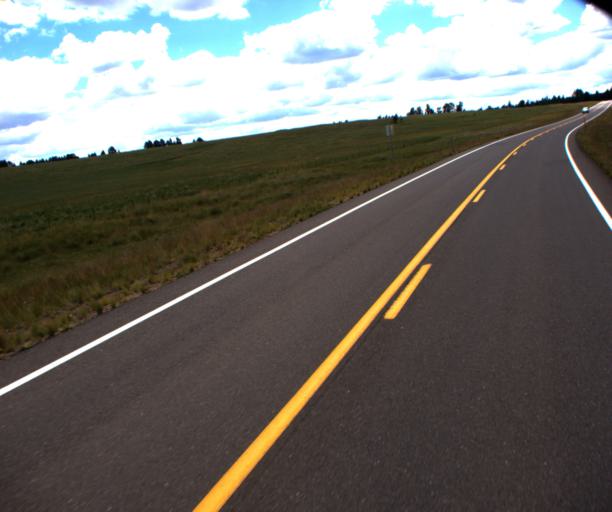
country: US
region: Arizona
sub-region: Apache County
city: Eagar
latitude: 33.9905
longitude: -109.5132
